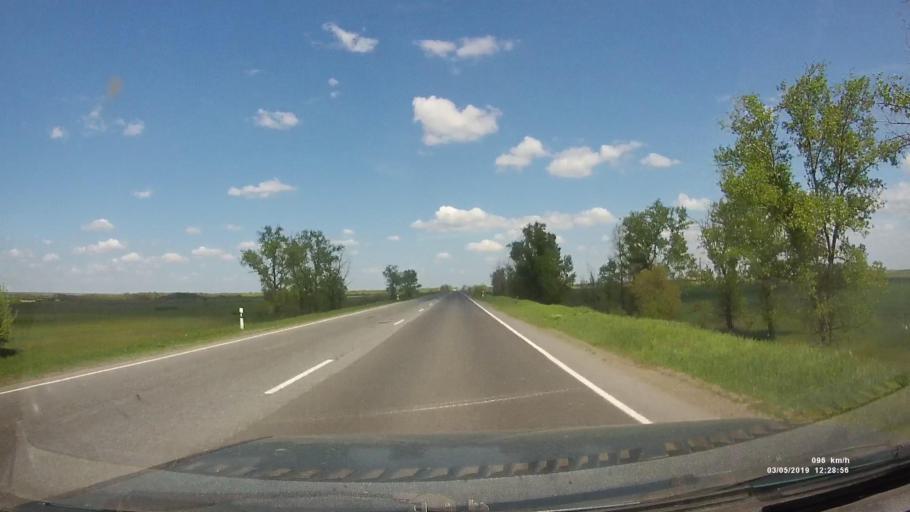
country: RU
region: Rostov
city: Semikarakorsk
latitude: 47.4803
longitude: 40.7319
